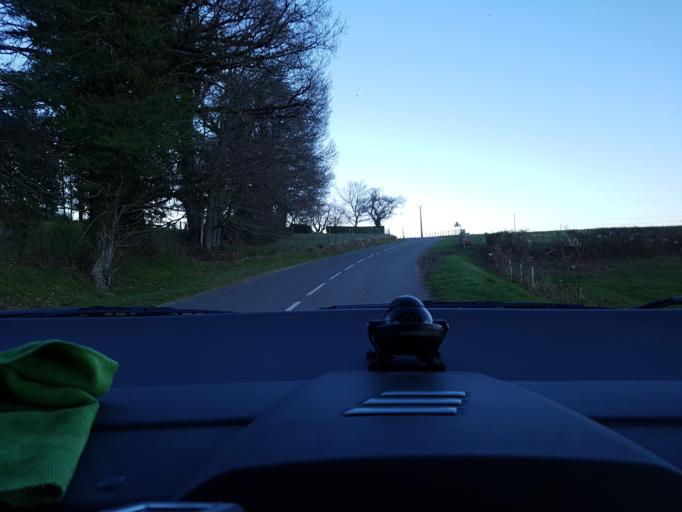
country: FR
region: Bourgogne
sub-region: Departement de Saone-et-Loire
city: Etang-sur-Arroux
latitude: 46.9193
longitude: 4.0857
